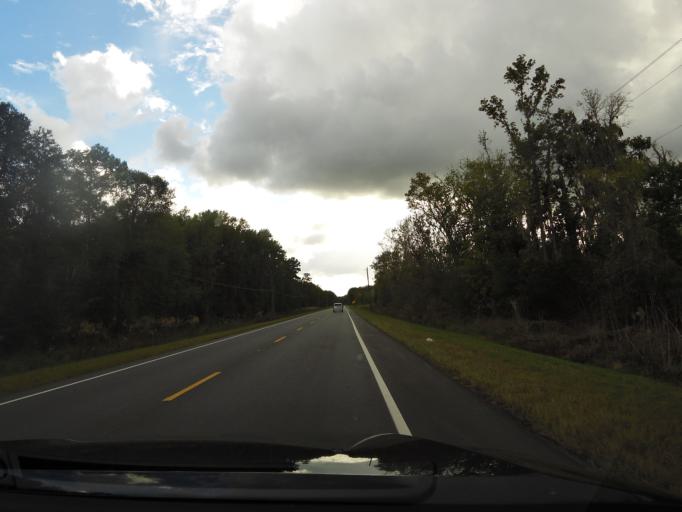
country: US
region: Georgia
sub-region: Liberty County
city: Midway
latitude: 31.8369
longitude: -81.4169
